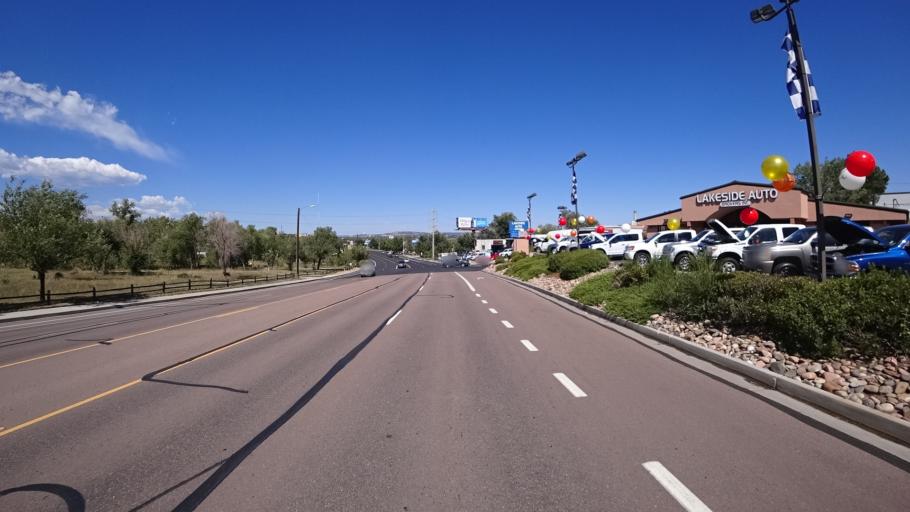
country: US
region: Colorado
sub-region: El Paso County
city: Colorado Springs
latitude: 38.8213
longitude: -104.8412
